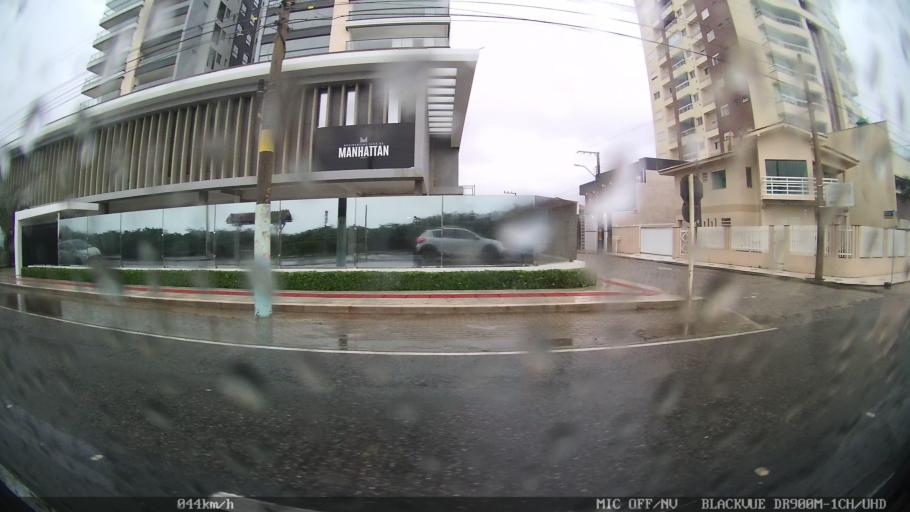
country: BR
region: Santa Catarina
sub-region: Navegantes
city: Navegantes
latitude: -26.8954
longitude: -48.6433
